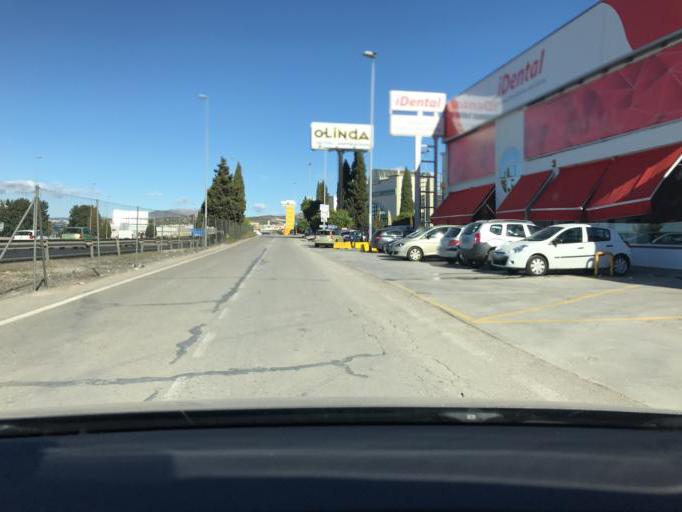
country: ES
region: Andalusia
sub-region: Provincia de Granada
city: Maracena
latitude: 37.2157
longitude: -3.6243
